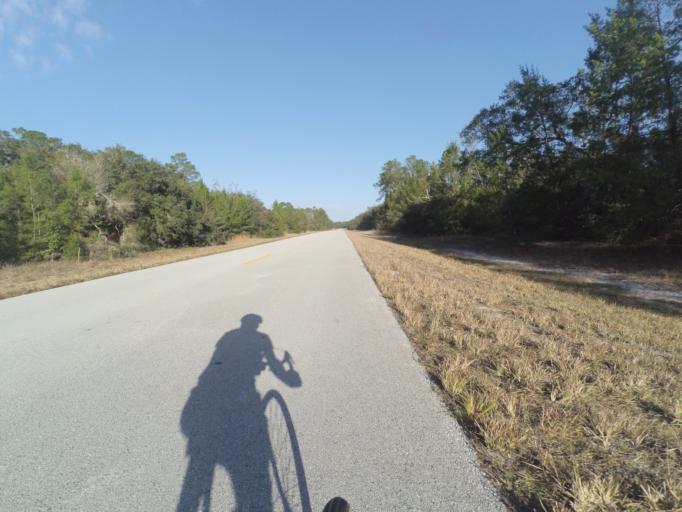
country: US
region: Florida
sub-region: Lake County
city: Astor
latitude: 29.1050
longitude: -81.5676
